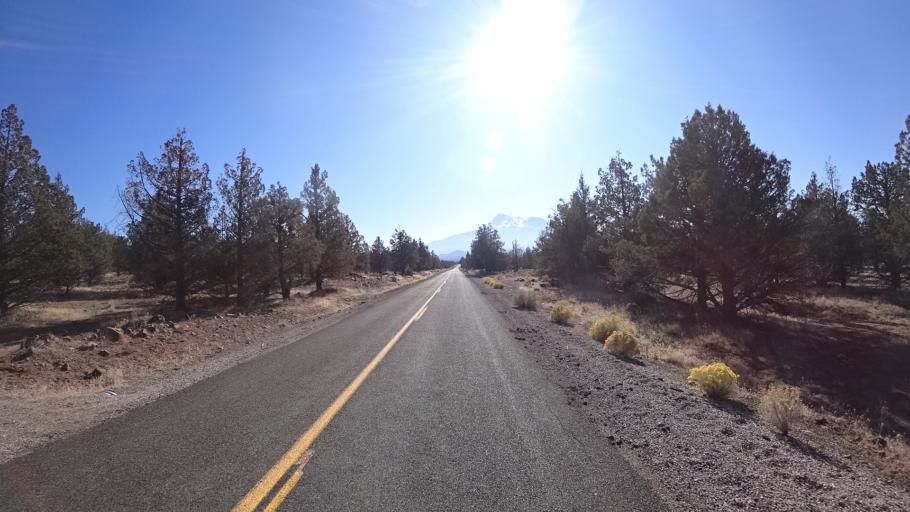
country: US
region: California
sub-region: Siskiyou County
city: Weed
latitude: 41.6106
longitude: -122.3121
